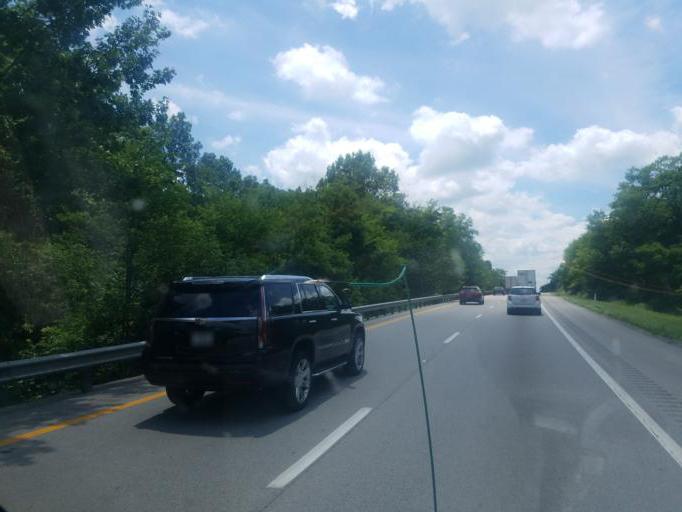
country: US
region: Kentucky
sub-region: Henry County
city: New Castle
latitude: 38.4736
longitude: -85.2759
